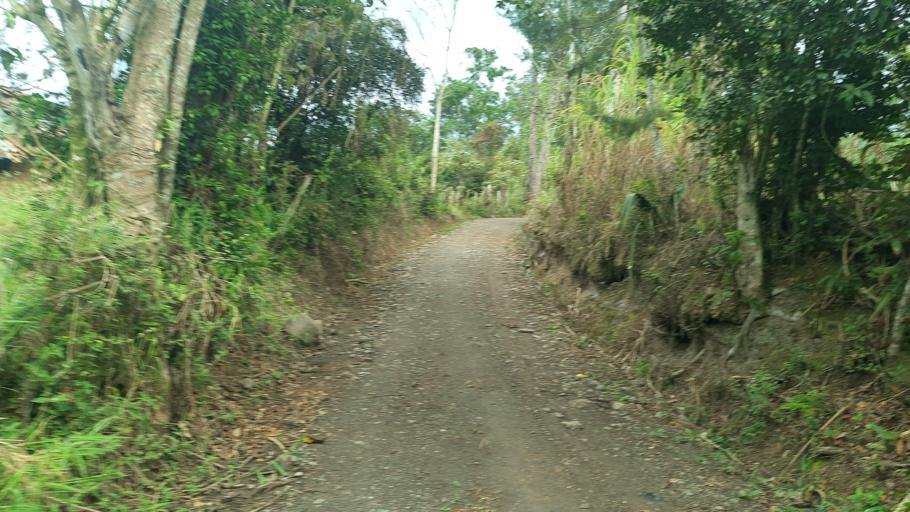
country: CO
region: Boyaca
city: Garagoa
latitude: 5.0820
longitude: -73.3784
